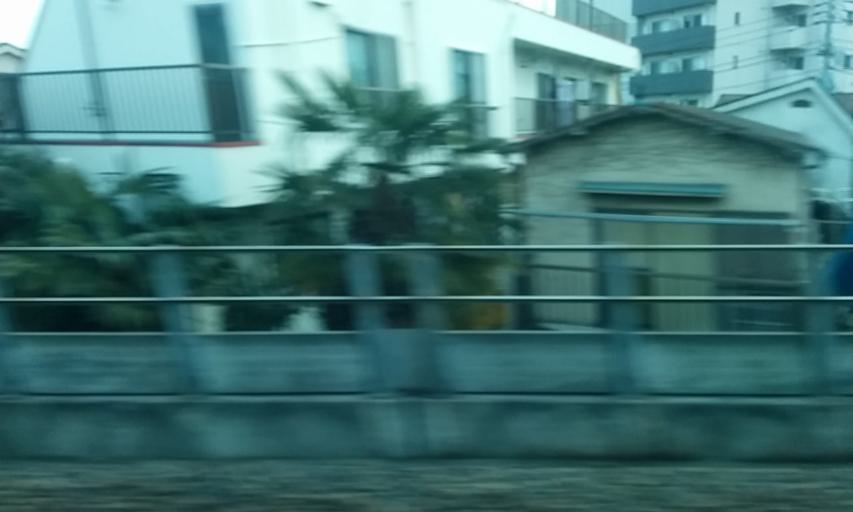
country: JP
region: Saitama
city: Kawaguchi
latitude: 35.7856
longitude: 139.7172
